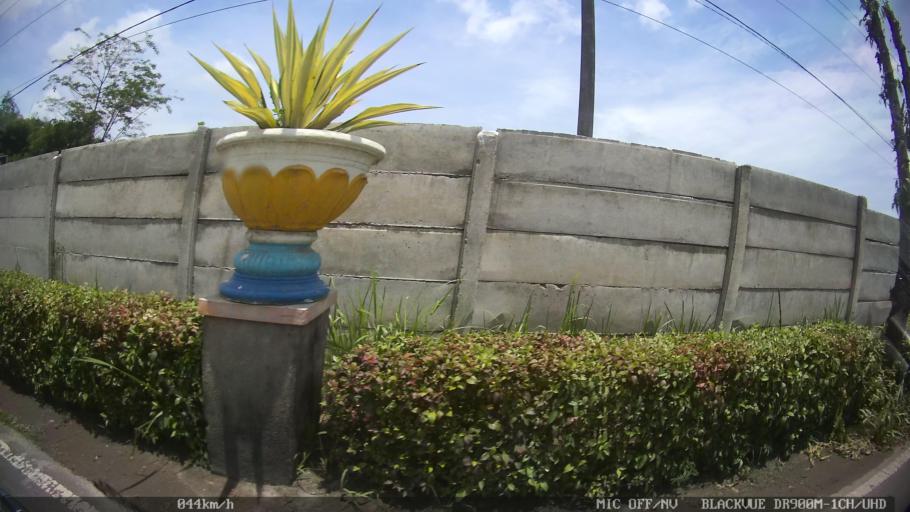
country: ID
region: North Sumatra
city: Percut
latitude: 3.5577
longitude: 98.8576
